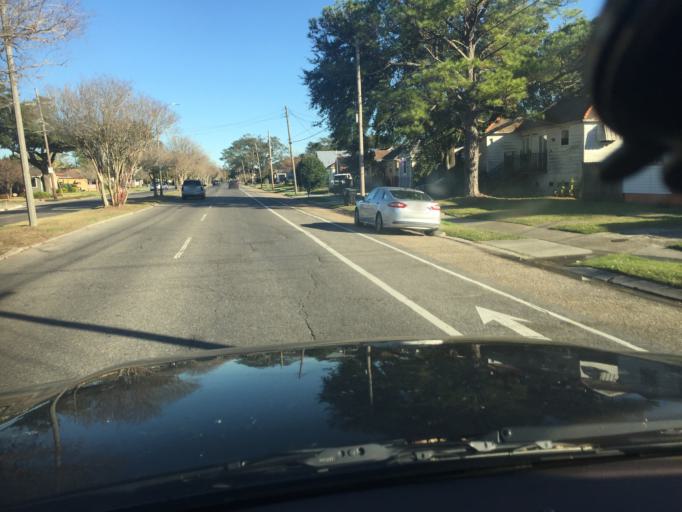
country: US
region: Louisiana
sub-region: Orleans Parish
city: New Orleans
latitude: 29.9888
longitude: -90.0807
